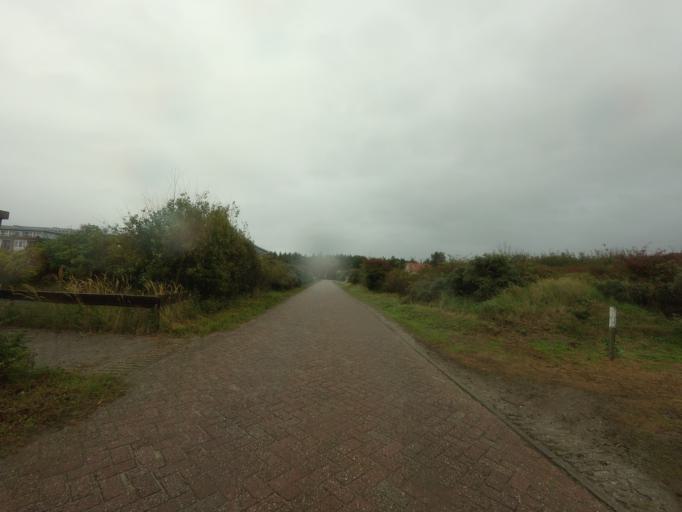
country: NL
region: Friesland
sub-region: Gemeente Ameland
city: Nes
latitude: 53.4564
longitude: 5.7755
